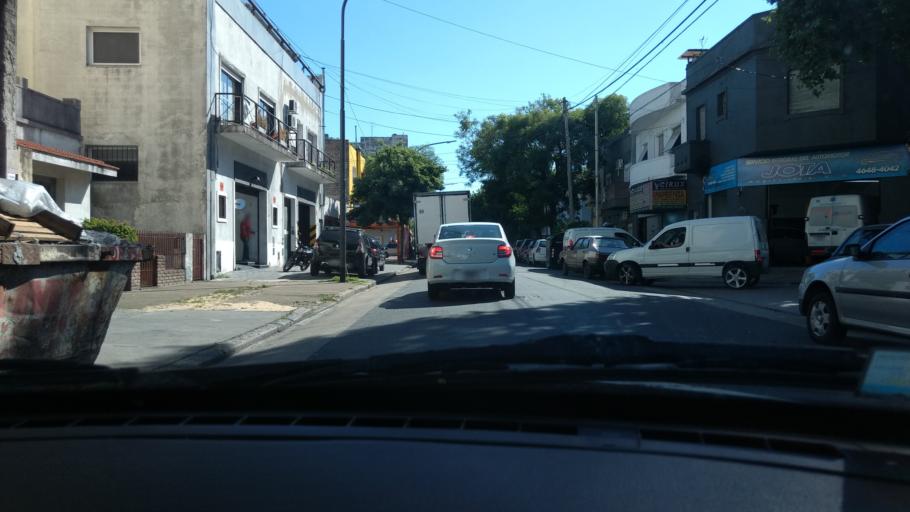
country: AR
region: Buenos Aires F.D.
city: Villa Santa Rita
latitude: -34.6150
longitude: -58.5123
